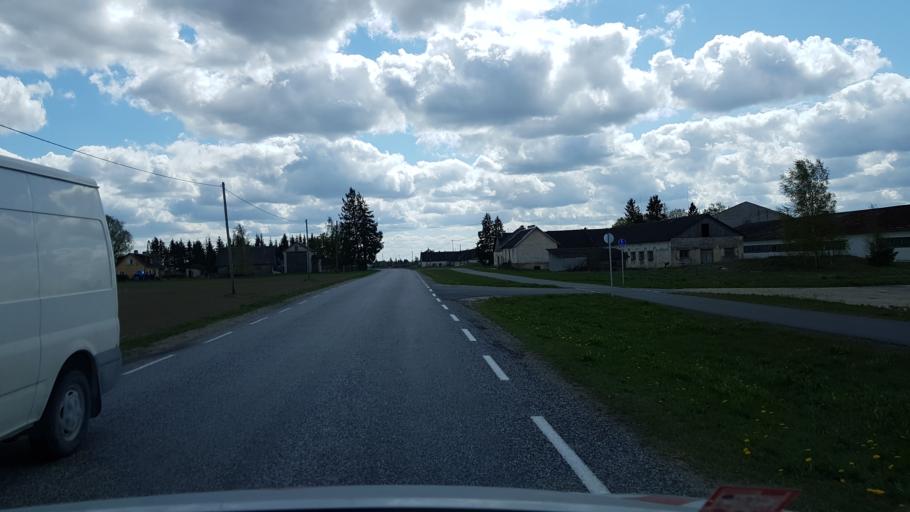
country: EE
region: Jogevamaa
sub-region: Poltsamaa linn
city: Poltsamaa
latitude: 58.6779
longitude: 25.9564
